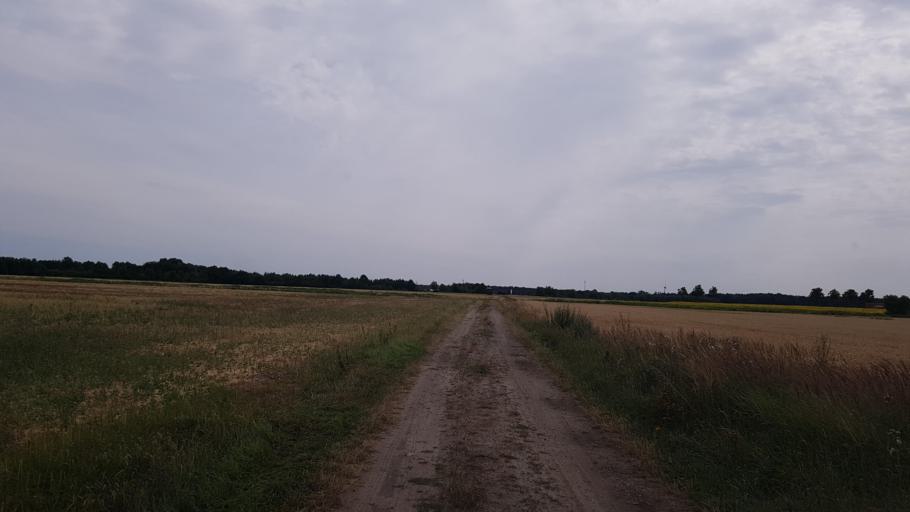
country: DE
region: Brandenburg
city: Bronkow
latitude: 51.5947
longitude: 13.9341
